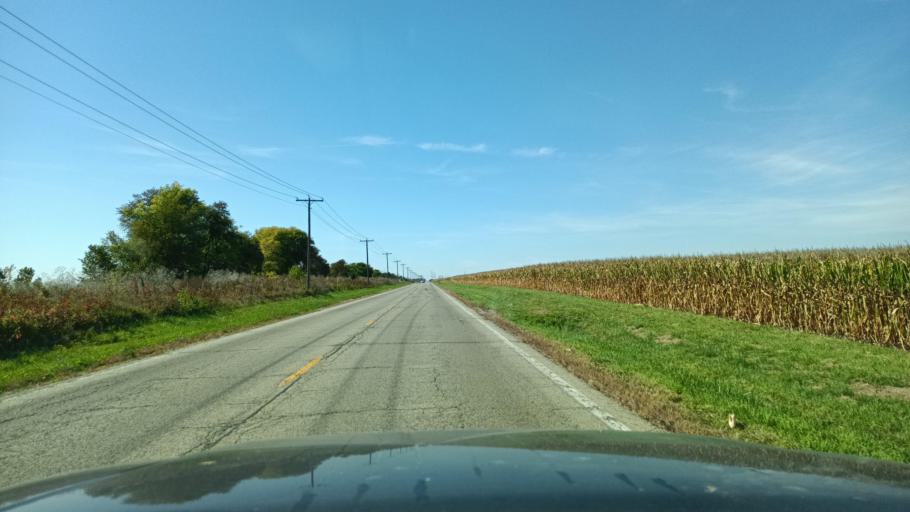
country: US
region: Illinois
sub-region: Champaign County
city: Mahomet
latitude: 40.2007
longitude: -88.4496
